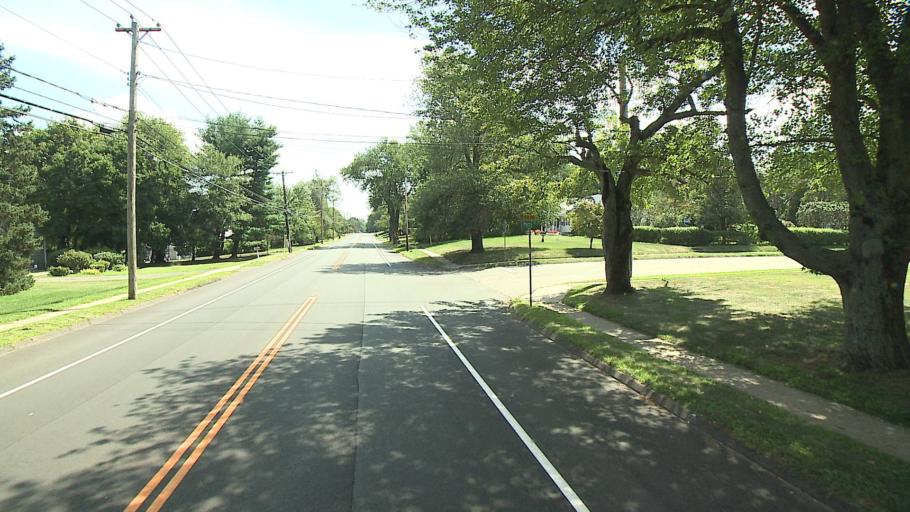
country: US
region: Connecticut
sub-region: Fairfield County
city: Stratford
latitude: 41.2259
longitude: -73.1521
